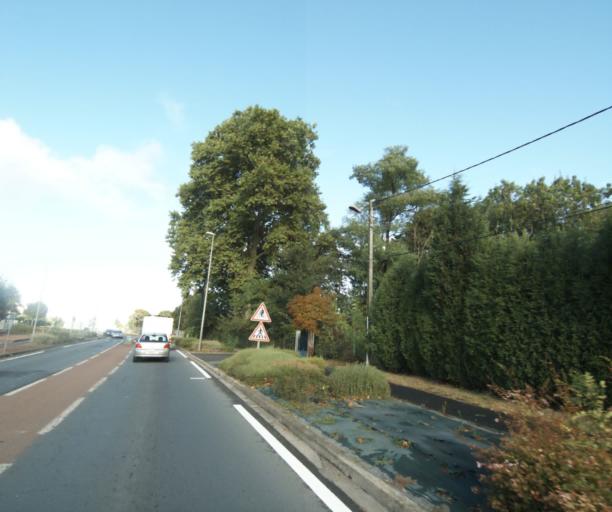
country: FR
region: Poitou-Charentes
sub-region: Departement de la Charente-Maritime
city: Tonnay-Charente
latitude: 45.9506
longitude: -0.9288
